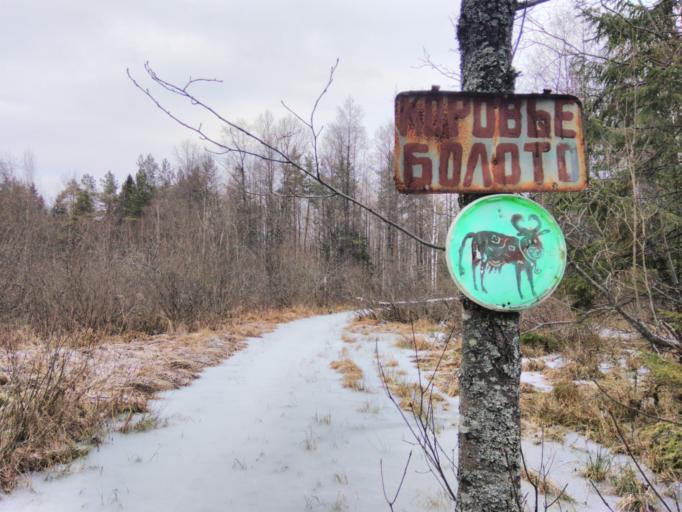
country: RU
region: Vladimir
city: Vorsha
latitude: 55.9752
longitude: 40.1131
